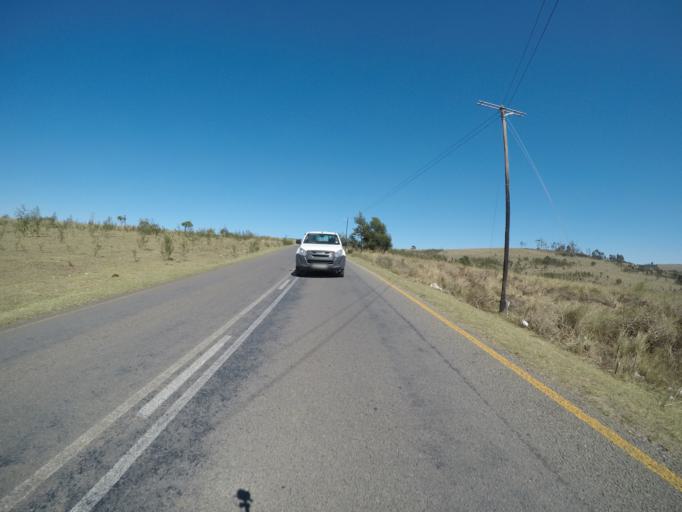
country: ZA
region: Eastern Cape
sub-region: OR Tambo District Municipality
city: Mthatha
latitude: -31.8067
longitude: 28.7602
